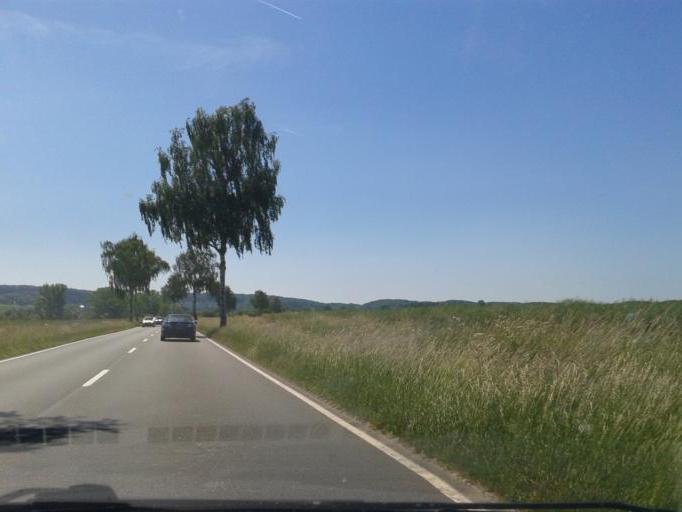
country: DE
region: North Rhine-Westphalia
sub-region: Regierungsbezirk Detmold
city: Blomberg
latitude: 51.9244
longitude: 9.0481
